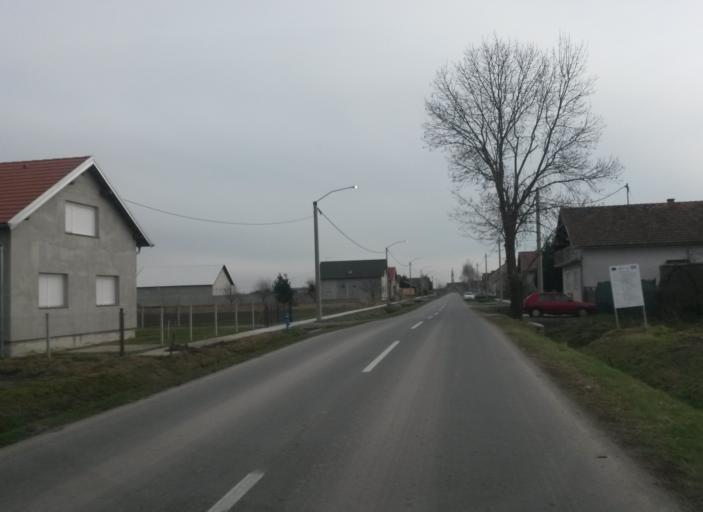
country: HR
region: Osjecko-Baranjska
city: Antunovac
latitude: 45.4913
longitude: 18.6263
